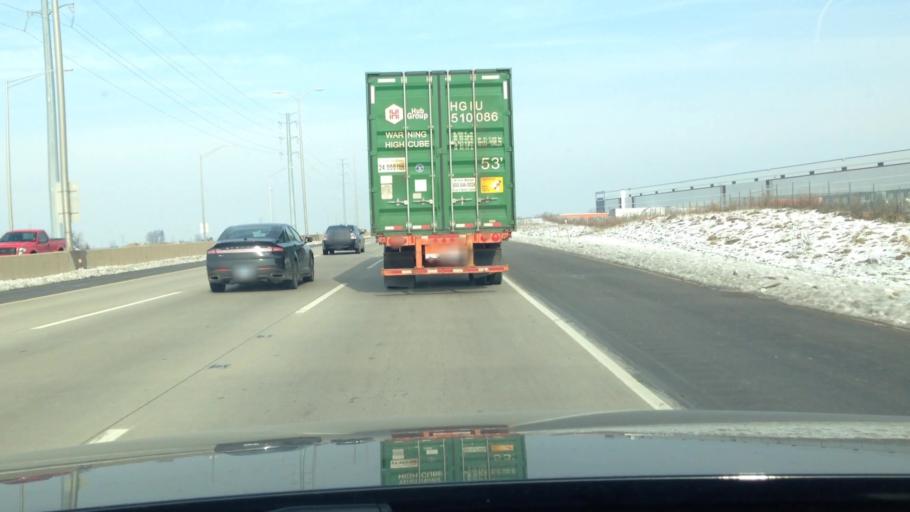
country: US
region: Illinois
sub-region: Will County
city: Lockport
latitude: 41.6187
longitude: -88.0124
